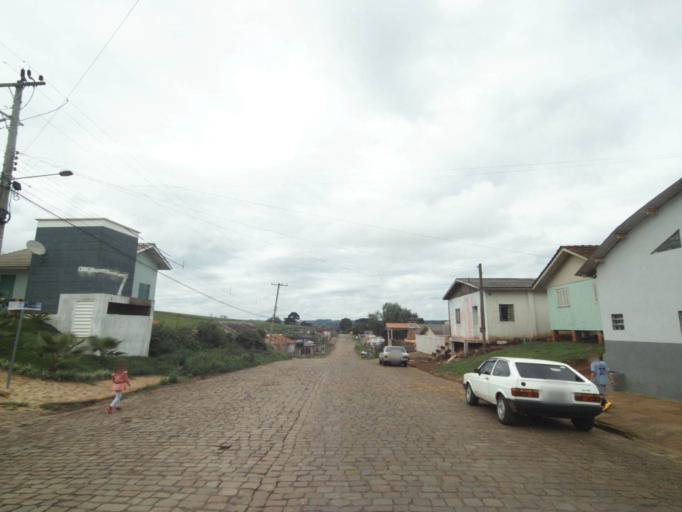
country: BR
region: Rio Grande do Sul
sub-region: Lagoa Vermelha
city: Lagoa Vermelha
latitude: -28.2164
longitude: -51.5352
